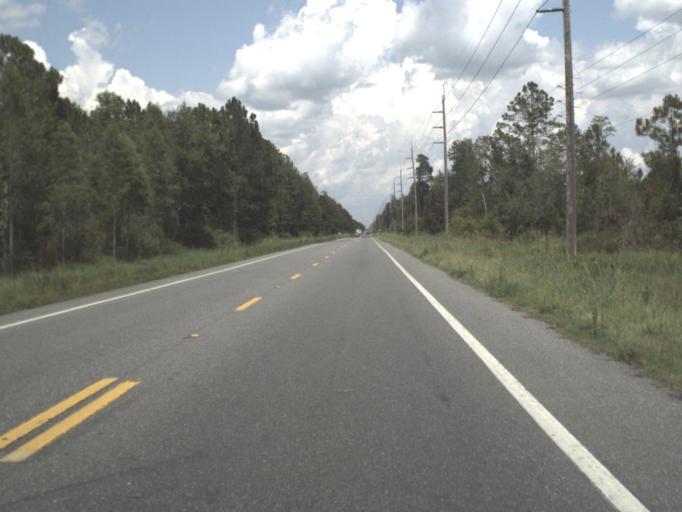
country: US
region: Florida
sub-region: Gilchrist County
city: Trenton
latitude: 29.6197
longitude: -82.7709
